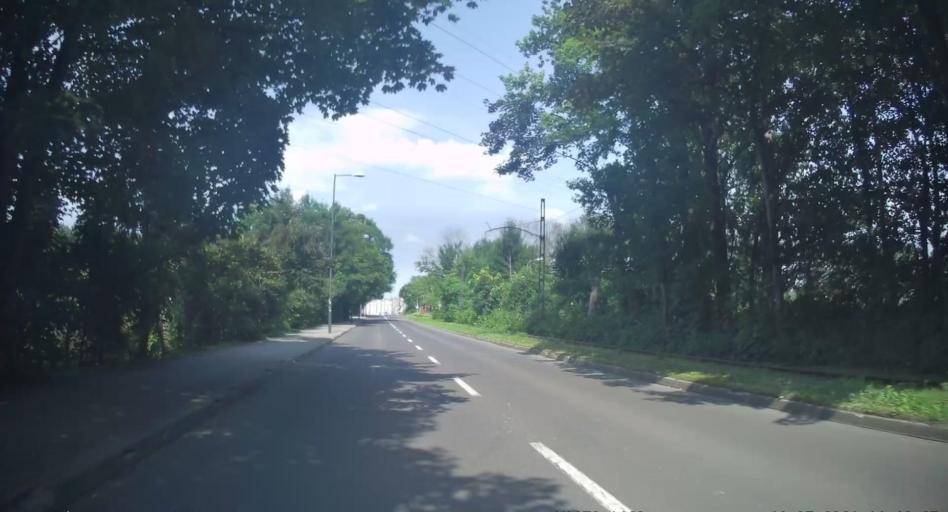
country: PL
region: Silesian Voivodeship
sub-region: Swietochlowice
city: Swietochlowice
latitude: 50.3192
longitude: 18.9232
